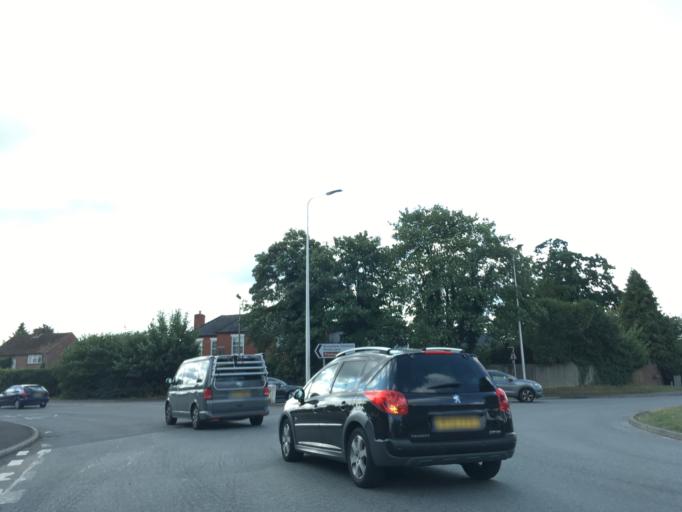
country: GB
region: England
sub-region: West Berkshire
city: Greenham
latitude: 51.3847
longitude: -1.3206
